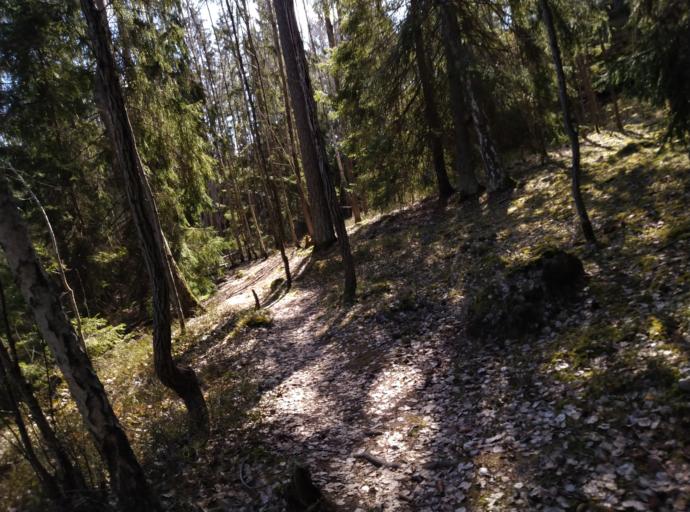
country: SE
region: Stockholm
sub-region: Nacka Kommun
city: Fisksatra
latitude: 59.2956
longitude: 18.2478
